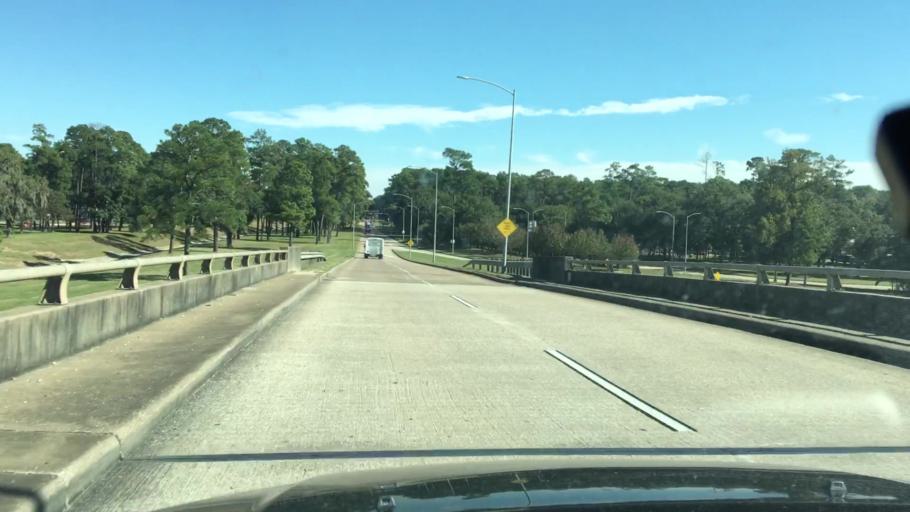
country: US
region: Texas
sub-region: Harris County
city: Humble
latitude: 29.9847
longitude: -95.3249
